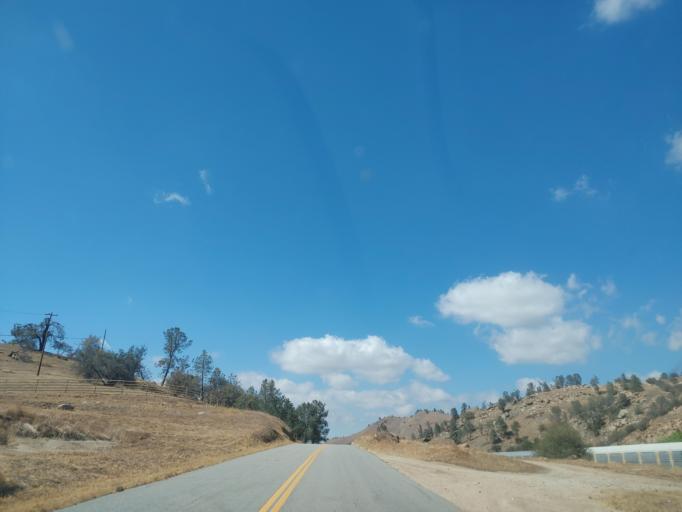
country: US
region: California
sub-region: Kern County
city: Bear Valley Springs
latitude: 35.2151
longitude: -118.5547
